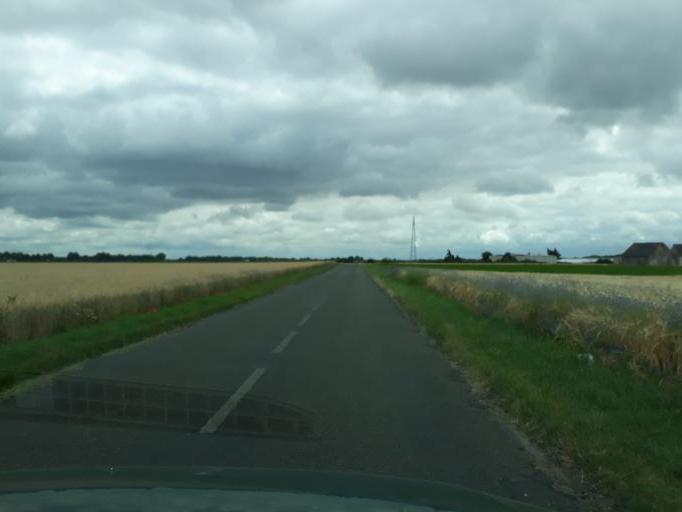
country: FR
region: Centre
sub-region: Departement du Loiret
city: Saint-Denis-en-Val
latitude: 47.8615
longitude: 1.9510
